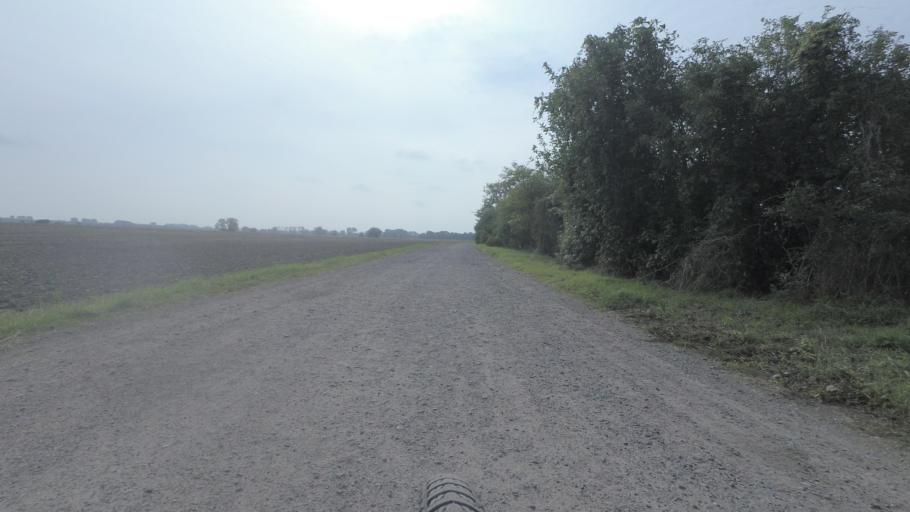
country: DE
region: Brandenburg
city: Rangsdorf
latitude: 52.2776
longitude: 13.3872
